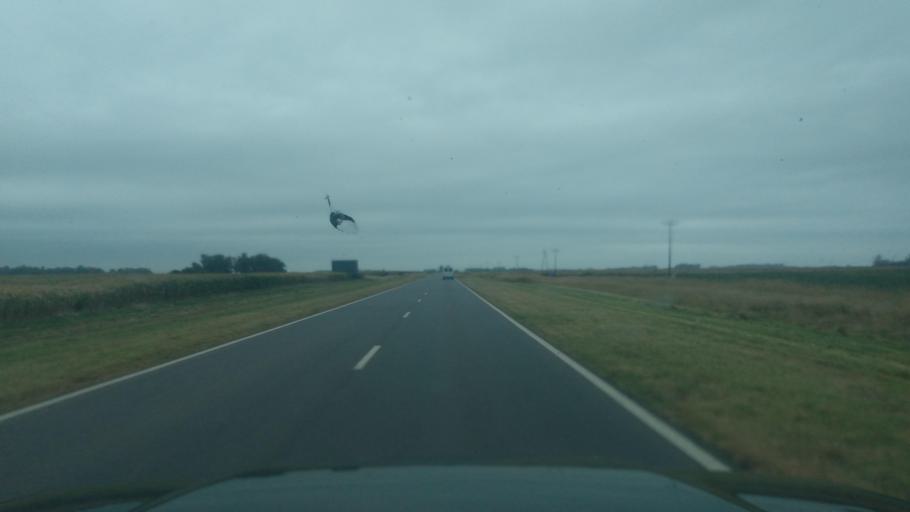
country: AR
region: Buenos Aires
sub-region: Partido de Nueve de Julio
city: Nueve de Julio
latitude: -35.3850
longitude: -60.7312
